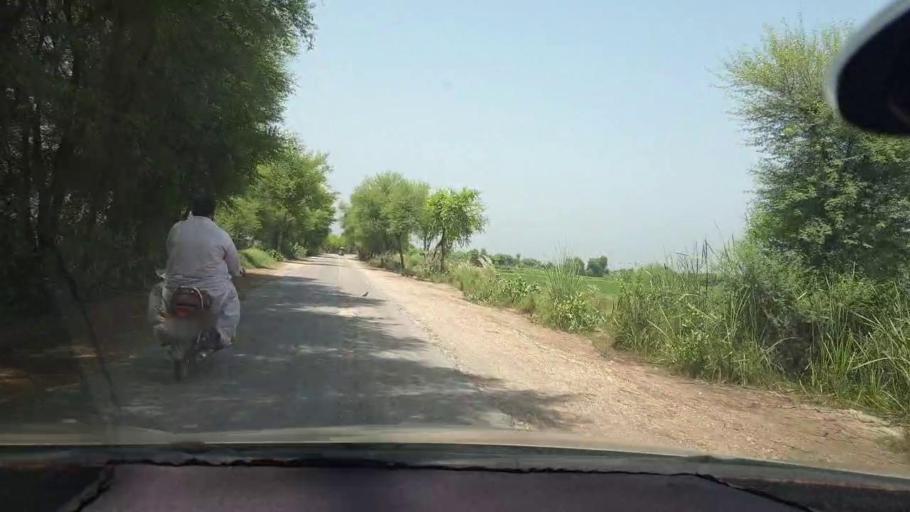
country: PK
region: Sindh
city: Kambar
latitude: 27.6391
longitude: 67.9763
